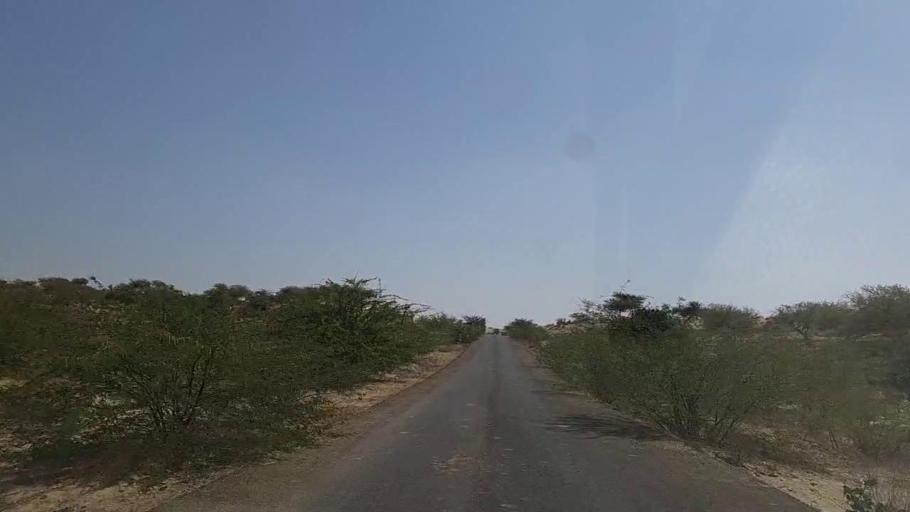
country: PK
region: Sindh
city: Diplo
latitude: 24.4855
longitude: 69.4489
